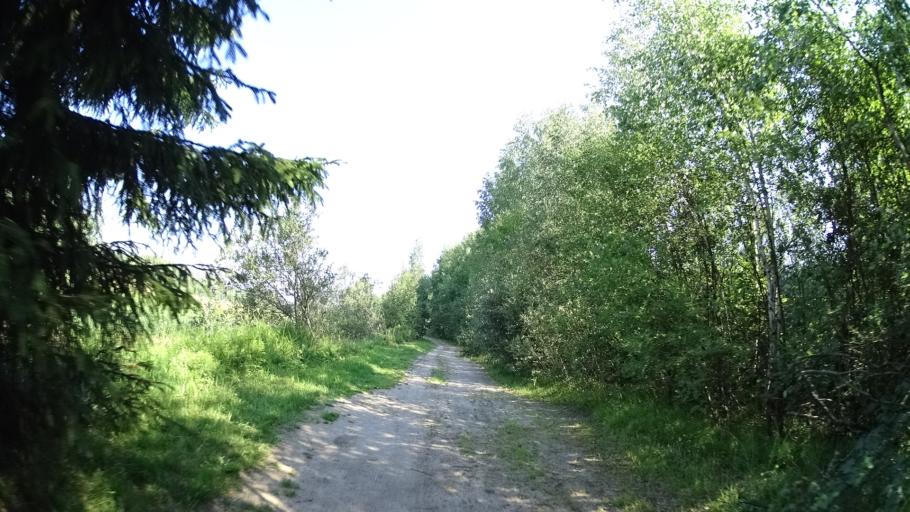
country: FI
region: Uusimaa
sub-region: Helsinki
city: Kerava
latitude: 60.3522
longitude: 25.1260
